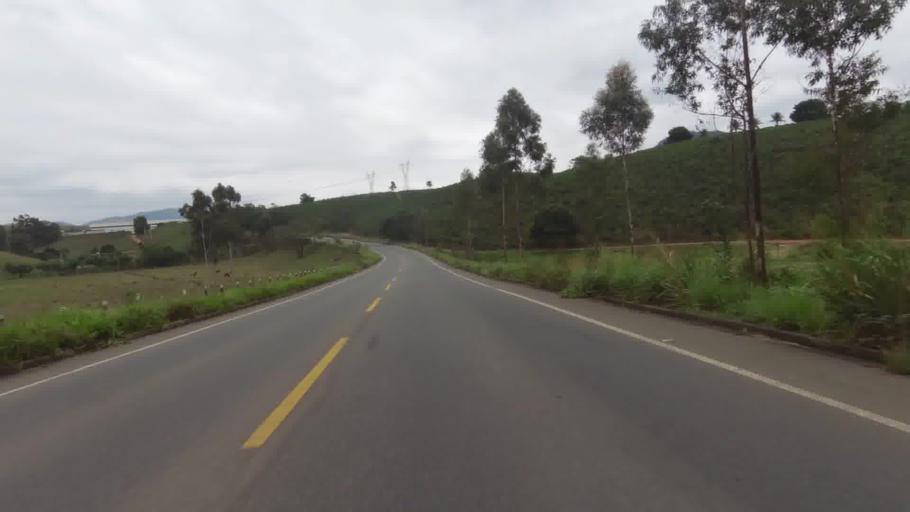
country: BR
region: Espirito Santo
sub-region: Piuma
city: Piuma
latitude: -20.7874
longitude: -40.7522
